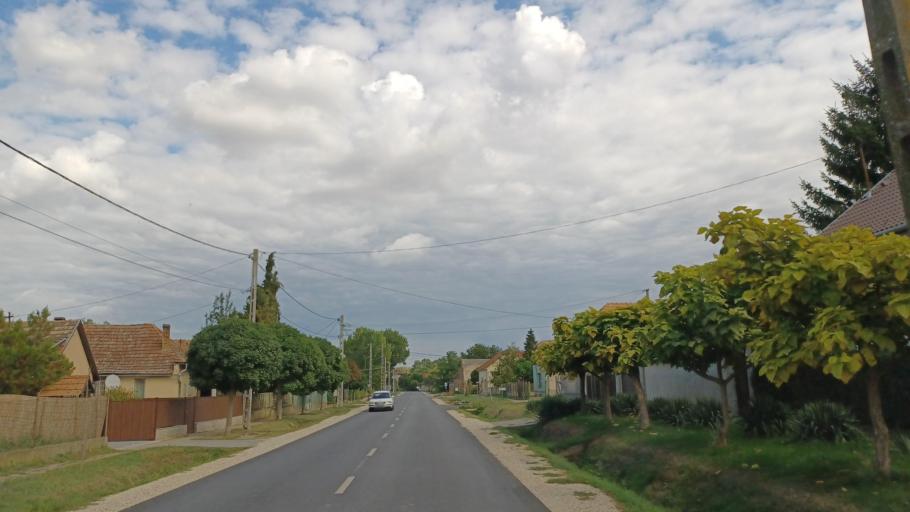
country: HU
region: Tolna
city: Nagydorog
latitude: 46.6173
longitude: 18.6564
